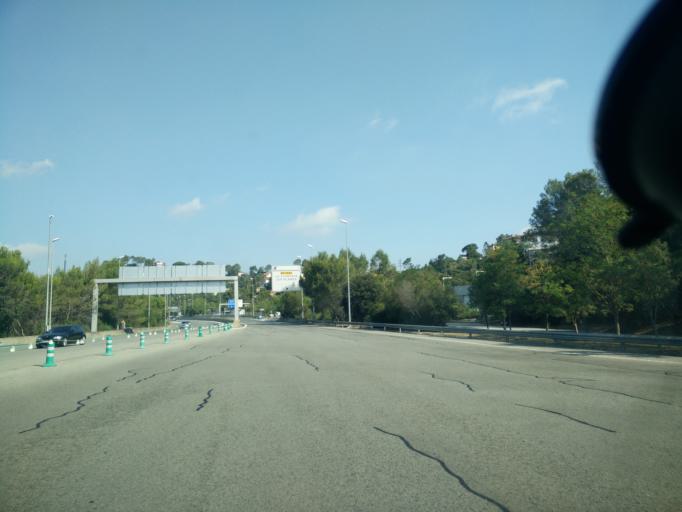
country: ES
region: Catalonia
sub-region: Provincia de Barcelona
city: Sant Cugat del Valles
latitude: 41.4380
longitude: 2.0750
